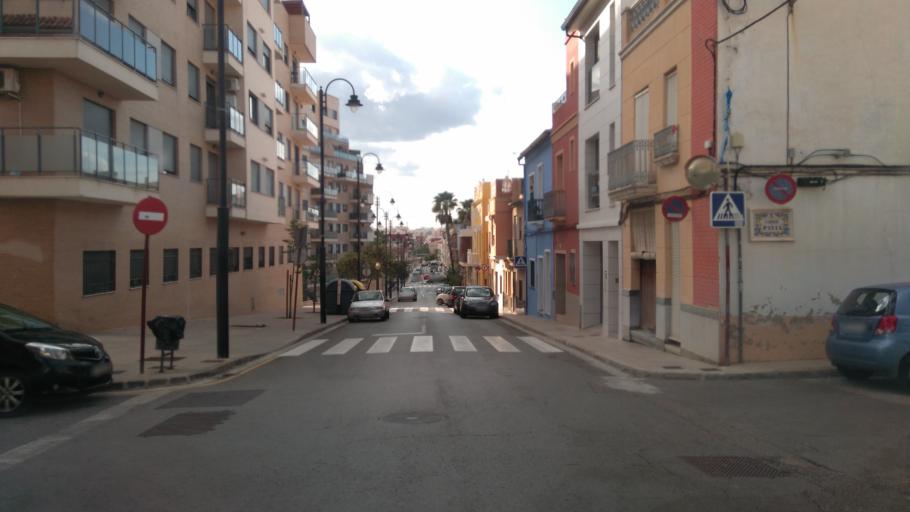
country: ES
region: Valencia
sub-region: Provincia de Valencia
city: Alzira
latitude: 39.1534
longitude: -0.4242
